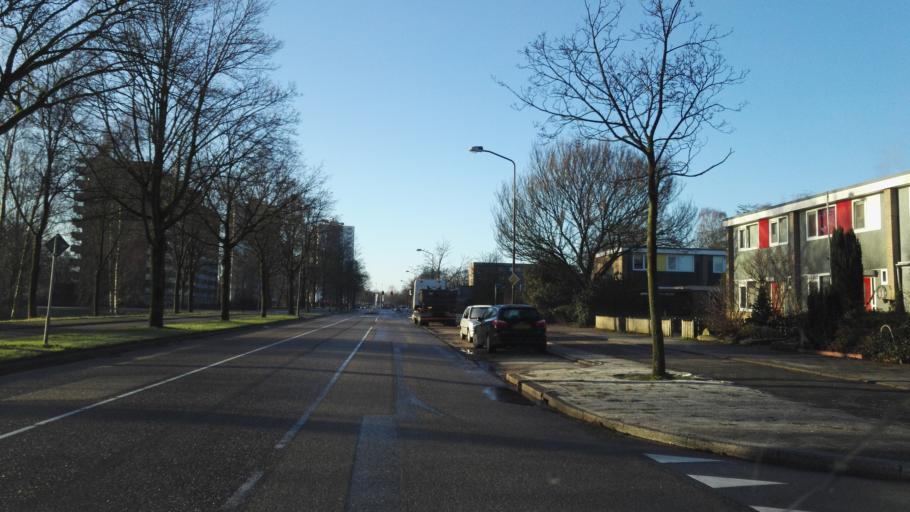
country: NL
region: Gelderland
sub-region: Gemeente Apeldoorn
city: Apeldoorn
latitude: 52.2253
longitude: 5.9971
